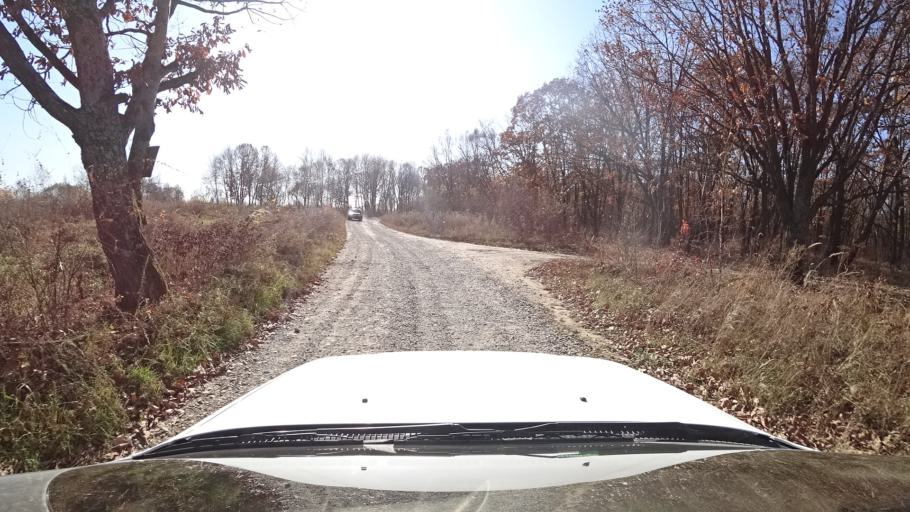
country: RU
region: Primorskiy
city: Dal'nerechensk
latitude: 45.8826
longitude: 133.7354
